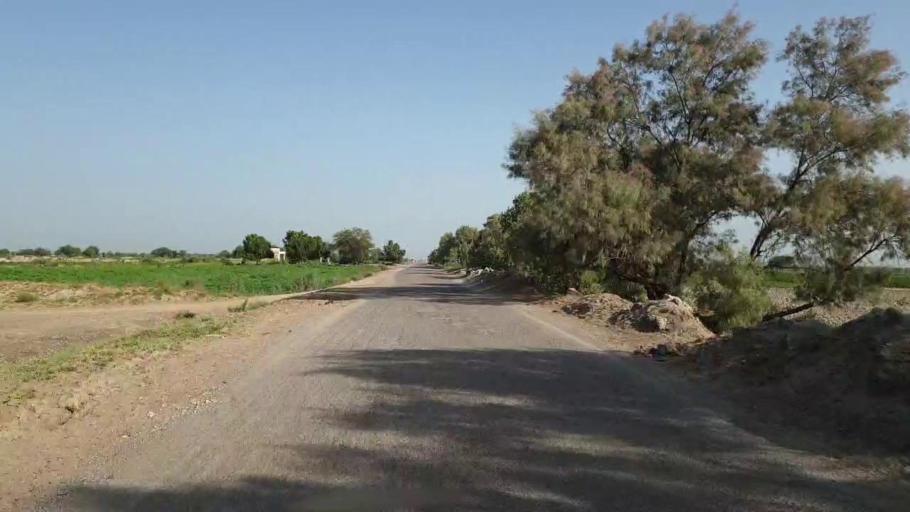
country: PK
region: Sindh
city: Nawabshah
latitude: 26.1565
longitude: 68.4456
